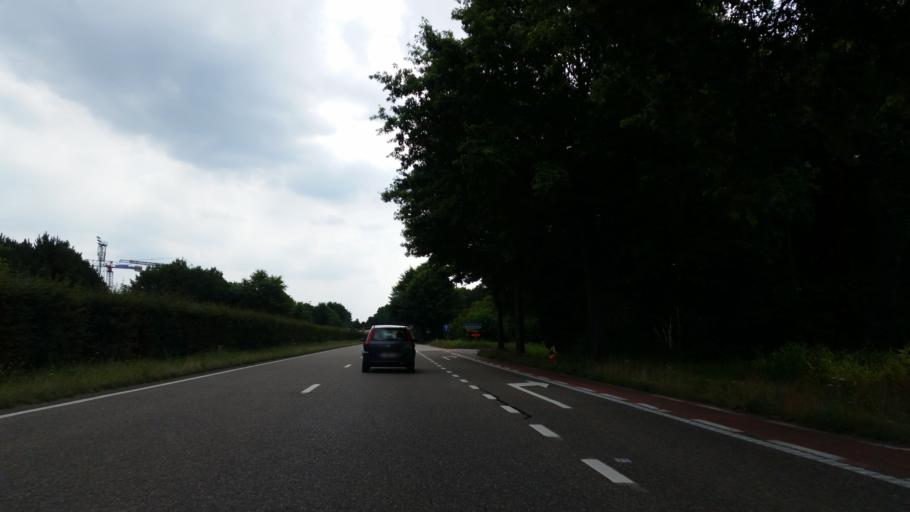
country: BE
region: Flanders
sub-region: Provincie Antwerpen
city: Geel
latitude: 51.1728
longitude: 4.9674
